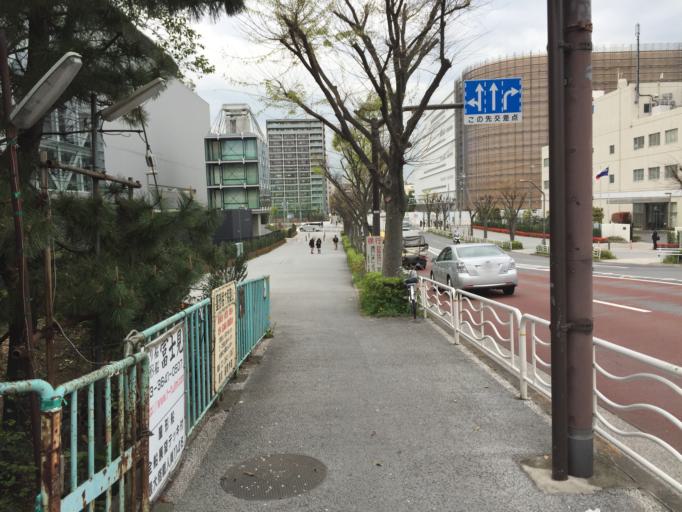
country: JP
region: Tokyo
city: Urayasu
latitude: 35.6627
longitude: 139.7985
